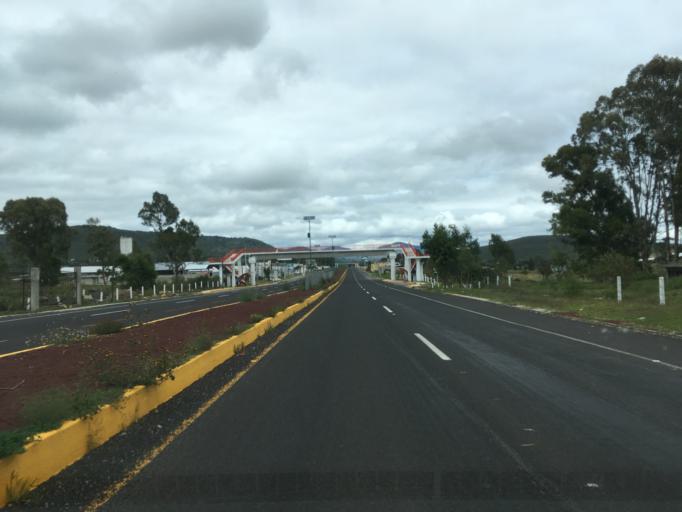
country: MX
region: Hidalgo
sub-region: Atotonilco el Grande
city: La Estancia
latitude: 20.3092
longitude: -98.6860
